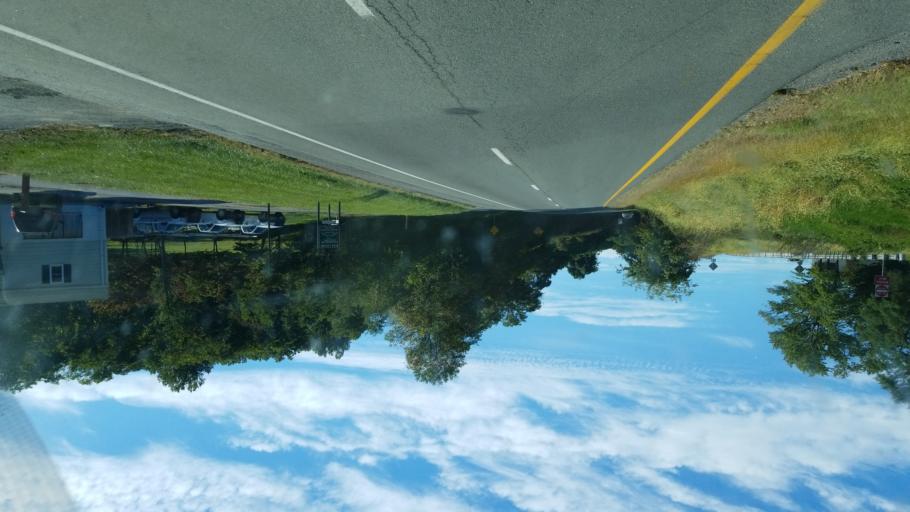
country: US
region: Virginia
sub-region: Warren County
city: Shenandoah Farms
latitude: 39.0152
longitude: -77.9639
